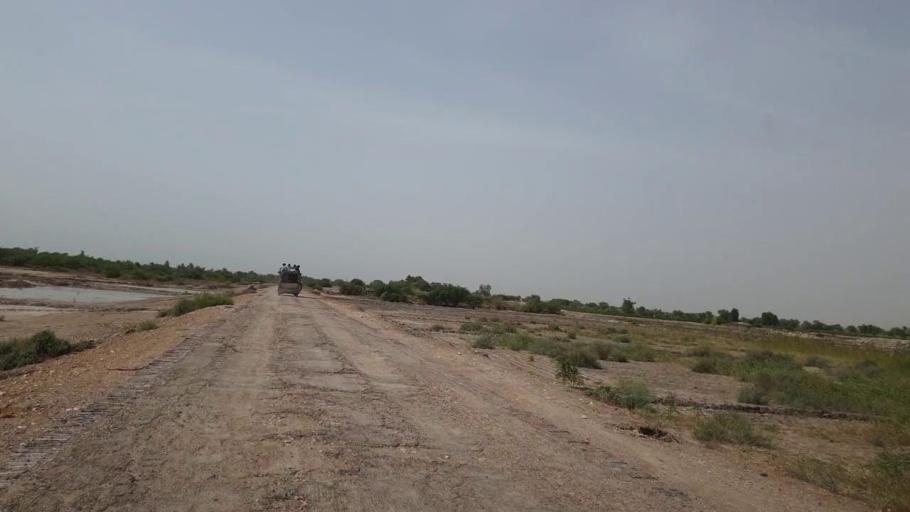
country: PK
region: Sindh
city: Bandhi
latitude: 26.5645
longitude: 68.3810
